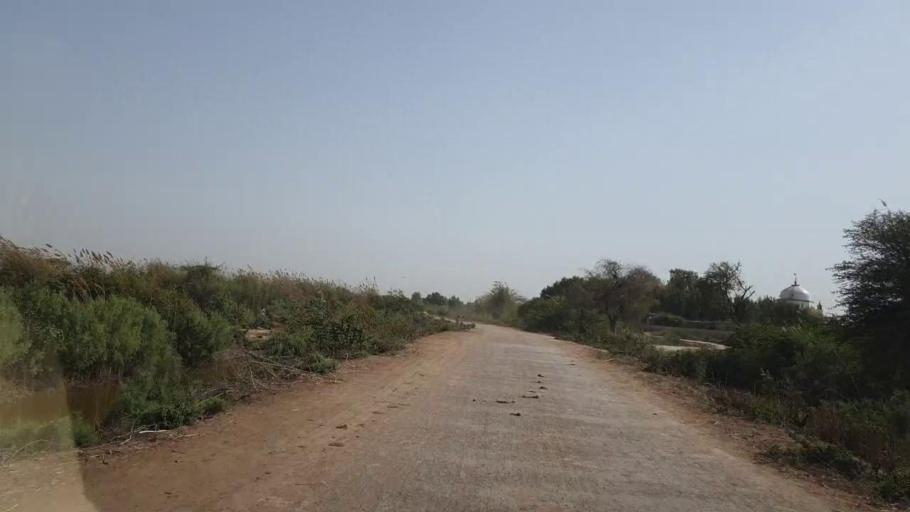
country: PK
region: Sindh
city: Rajo Khanani
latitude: 25.0528
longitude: 68.8411
